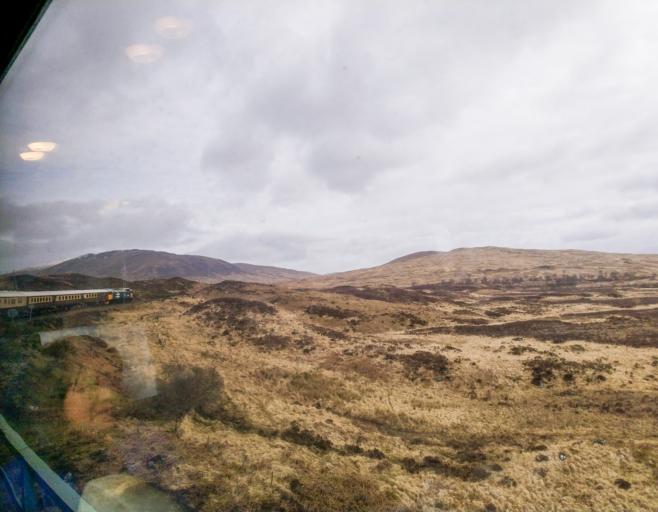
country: GB
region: Scotland
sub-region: Highland
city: Spean Bridge
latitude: 56.6904
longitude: -4.5768
